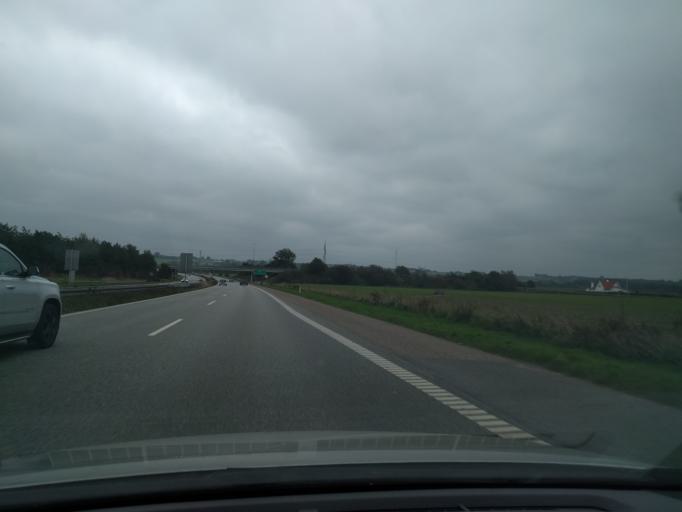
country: DK
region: Zealand
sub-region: Slagelse Kommune
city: Forlev
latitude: 55.3675
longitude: 11.2819
